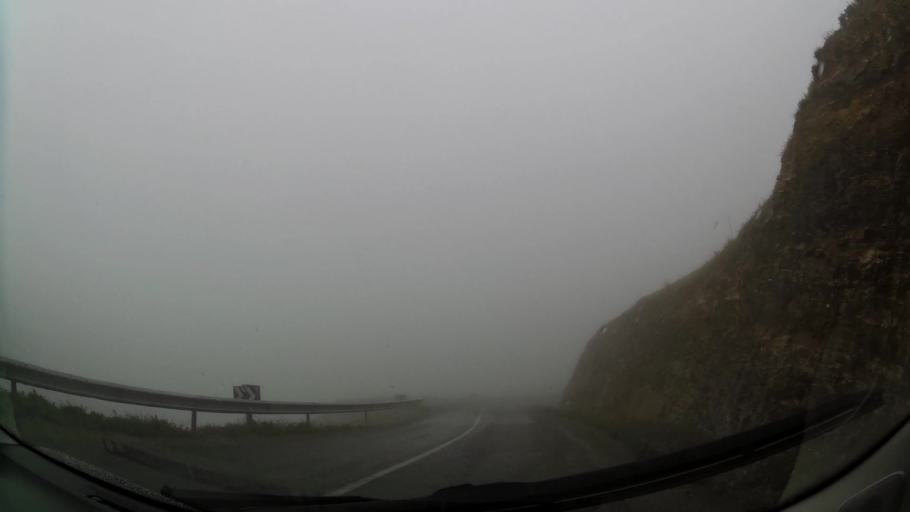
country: MA
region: Oriental
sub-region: Nador
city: Boudinar
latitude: 35.1047
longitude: -3.5560
